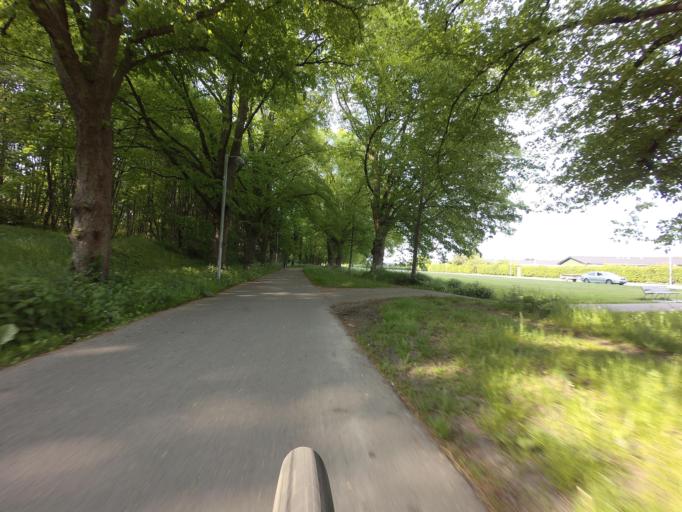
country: DK
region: Capital Region
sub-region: Brondby Kommune
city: Brondbyvester
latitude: 55.6562
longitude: 12.4256
